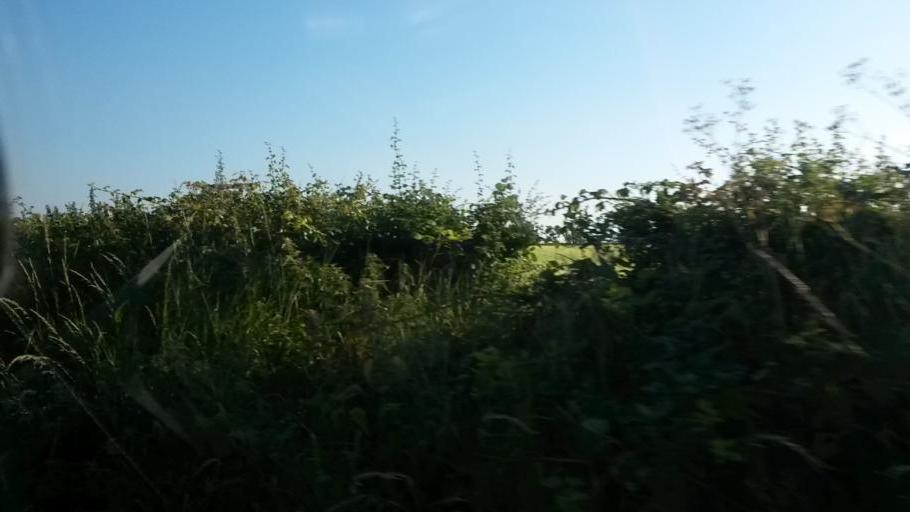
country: IE
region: Leinster
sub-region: An Mhi
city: Ashbourne
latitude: 53.5571
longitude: -6.3816
